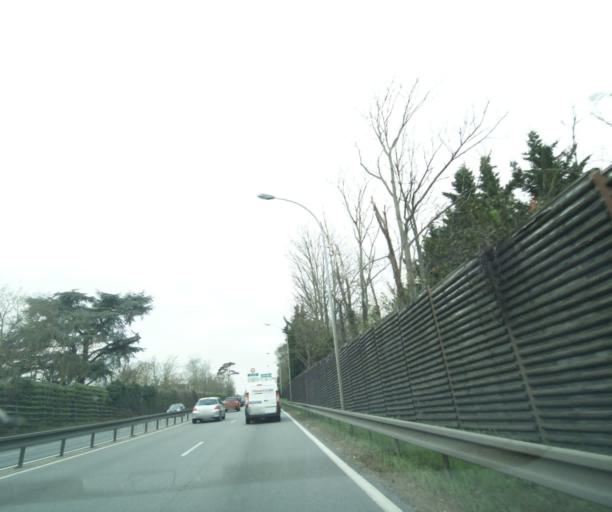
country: FR
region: Ile-de-France
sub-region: Departement des Yvelines
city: Saint-Germain-en-Laye
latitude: 48.8972
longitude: 2.0783
